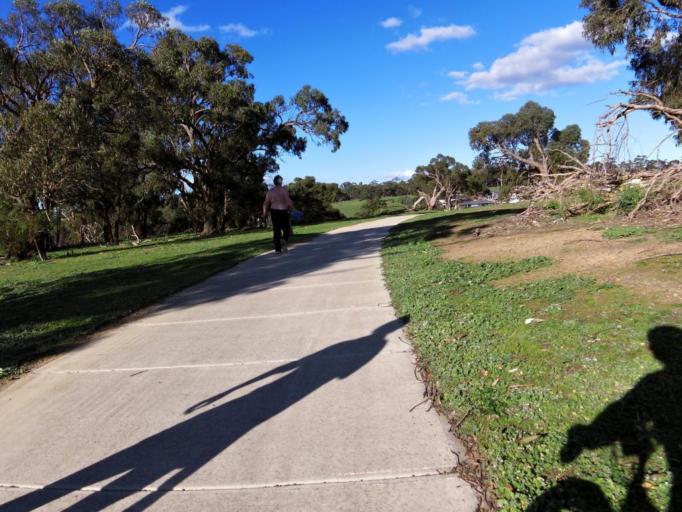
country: AU
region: Victoria
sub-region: Banyule
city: Watsonia North
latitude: -37.6837
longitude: 145.0884
